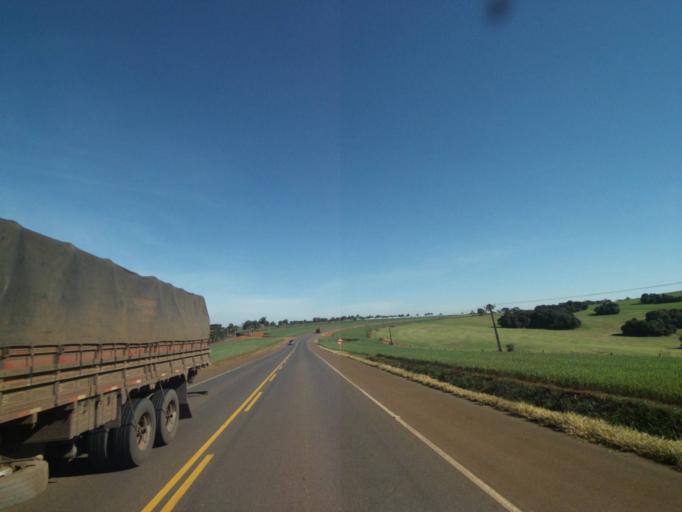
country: BR
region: Parana
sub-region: Tibagi
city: Tibagi
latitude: -24.4209
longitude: -50.3721
